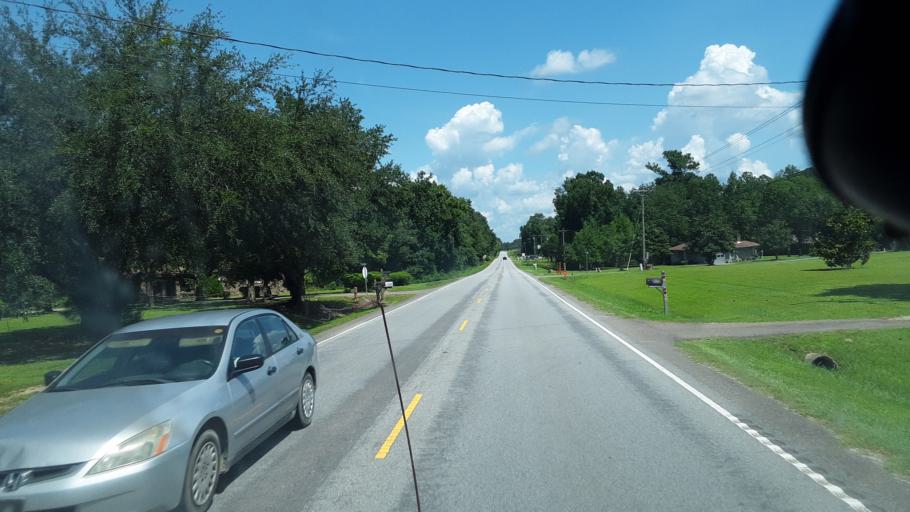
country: US
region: South Carolina
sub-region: Berkeley County
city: Moncks Corner
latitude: 33.2287
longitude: -79.9562
